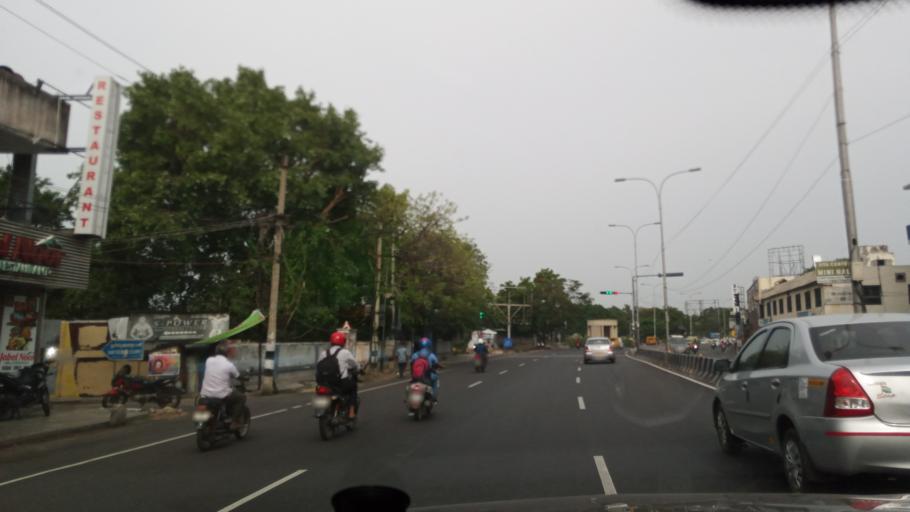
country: IN
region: Tamil Nadu
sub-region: Kancheepuram
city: Saint Thomas Mount
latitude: 13.0149
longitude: 80.1928
